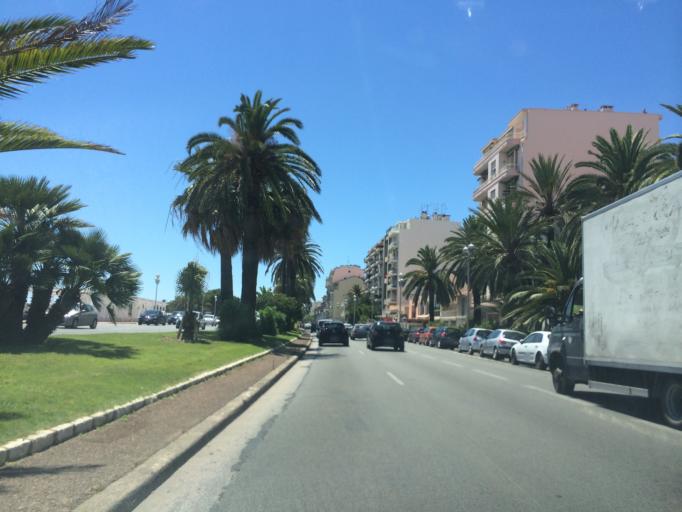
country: FR
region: Provence-Alpes-Cote d'Azur
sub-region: Departement des Alpes-Maritimes
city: Nice
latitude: 43.6810
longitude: 7.2315
